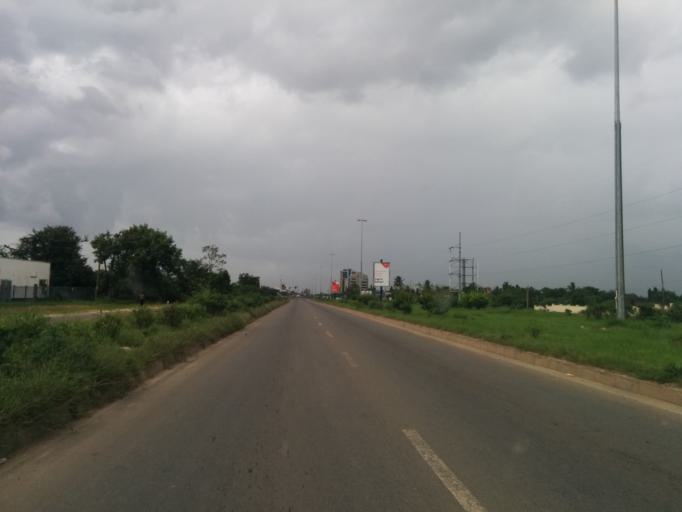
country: TZ
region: Dar es Salaam
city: Magomeni
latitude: -6.7804
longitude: 39.2161
